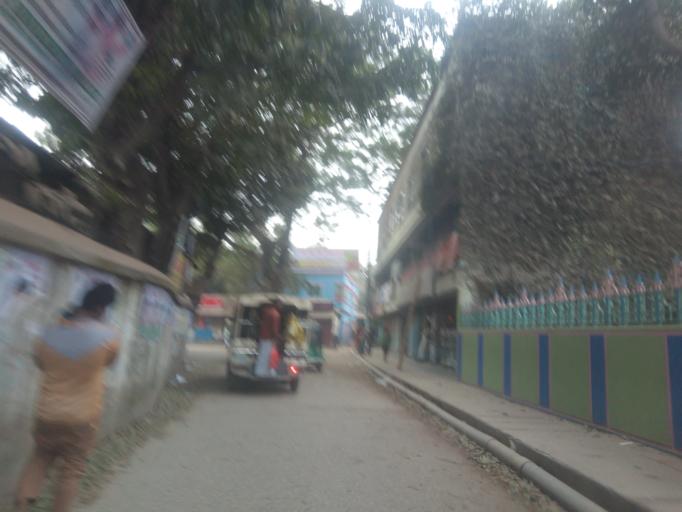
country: BD
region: Dhaka
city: Narayanganj
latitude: 23.5944
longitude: 90.5037
